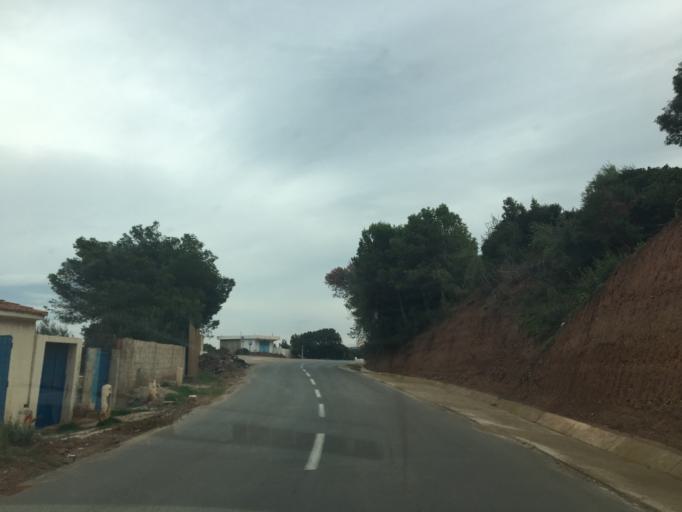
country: DZ
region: Tipaza
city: Tipasa
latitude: 36.6274
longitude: 2.4015
